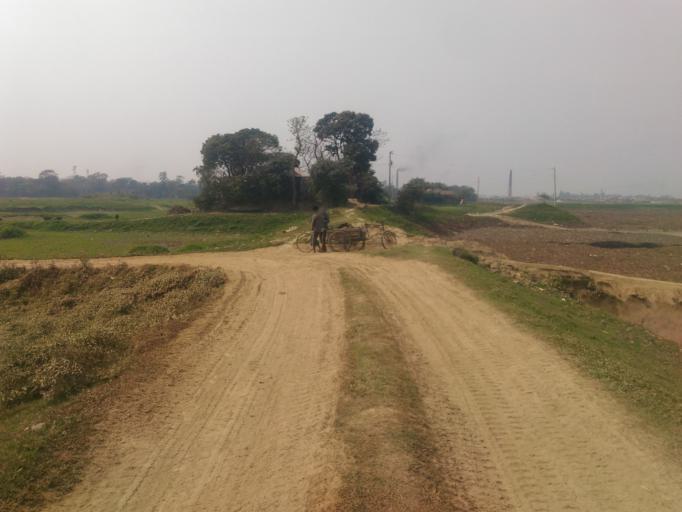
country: BD
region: Dhaka
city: Narayanganj
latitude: 23.6405
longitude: 90.4432
